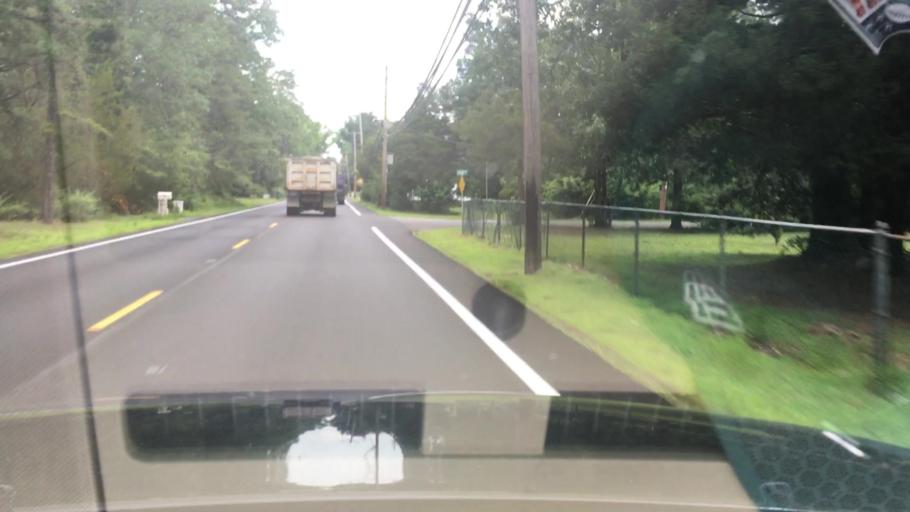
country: US
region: New Jersey
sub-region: Ocean County
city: Vista Center
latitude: 40.0997
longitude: -74.3858
